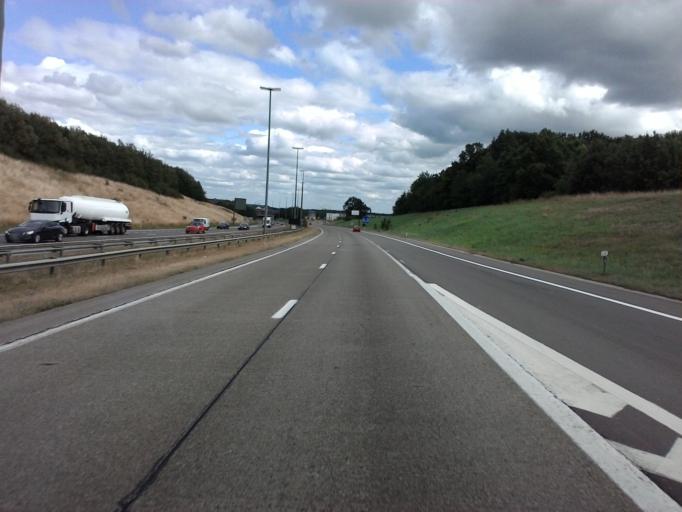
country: BE
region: Wallonia
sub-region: Province du Luxembourg
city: Arlon
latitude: 49.6476
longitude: 5.8221
